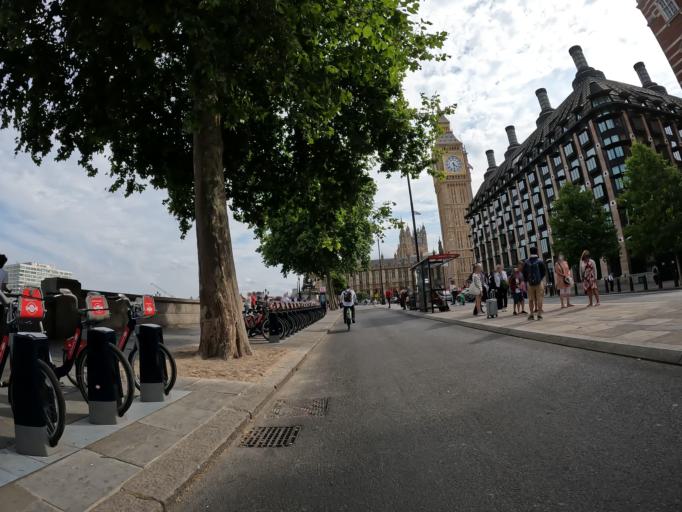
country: GB
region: England
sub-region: Greater London
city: Orpington
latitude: 51.3581
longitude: 0.0562
